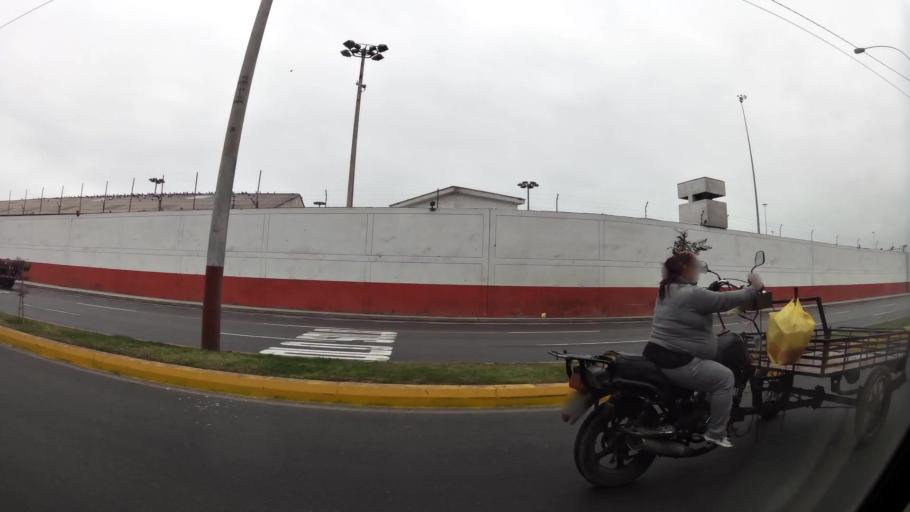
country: PE
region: Callao
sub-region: Callao
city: Callao
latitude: -12.0524
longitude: -77.1414
